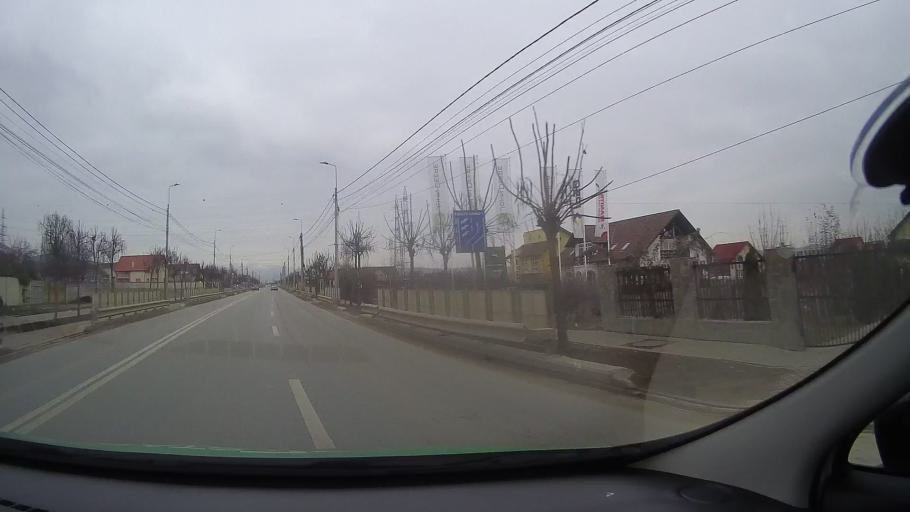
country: RO
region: Alba
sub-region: Municipiul Alba Iulia
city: Micesti
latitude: 46.0893
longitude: 23.5565
